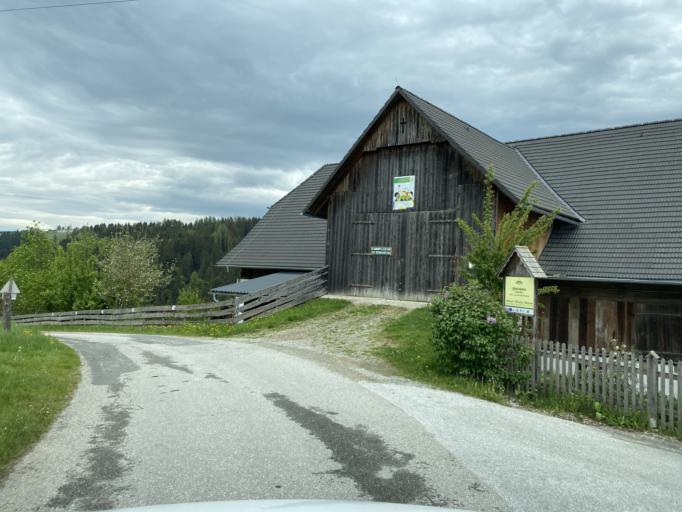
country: AT
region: Styria
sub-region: Politischer Bezirk Weiz
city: Koglhof
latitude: 47.3333
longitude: 15.6852
